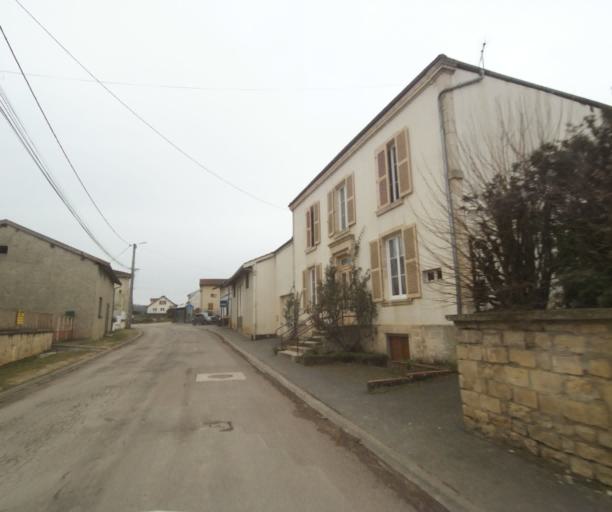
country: FR
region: Champagne-Ardenne
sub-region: Departement de la Haute-Marne
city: Wassy
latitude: 48.5434
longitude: 4.9803
